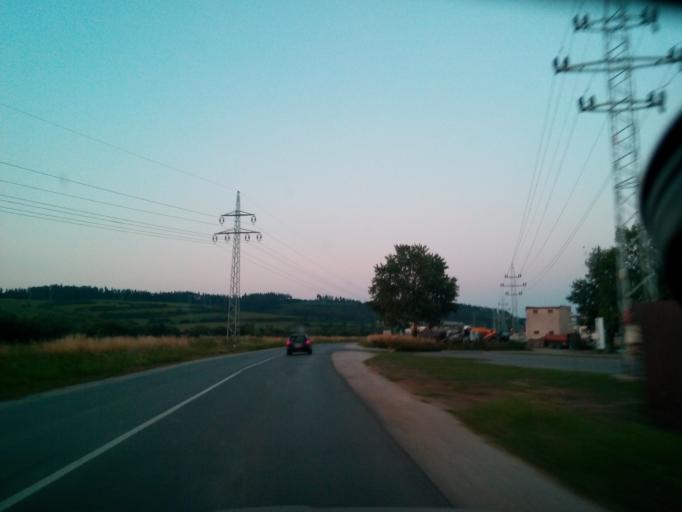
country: SK
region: Kosicky
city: Spisska Nova Ves
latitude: 48.9543
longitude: 20.5481
